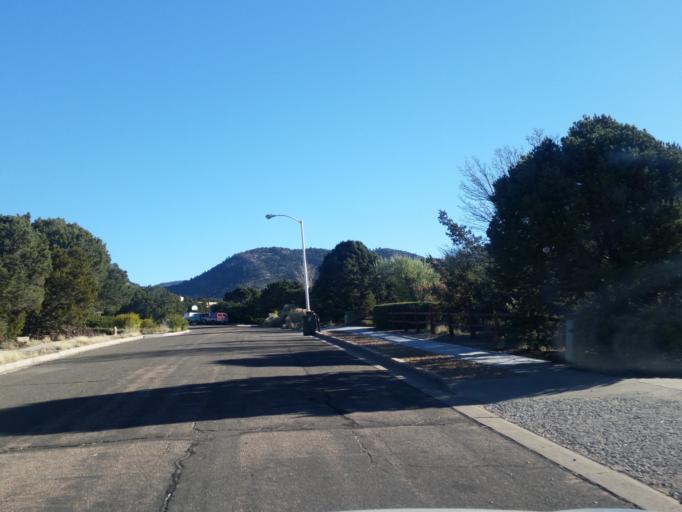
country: US
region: New Mexico
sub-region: Santa Fe County
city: Santa Fe
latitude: 35.6464
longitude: -105.9305
